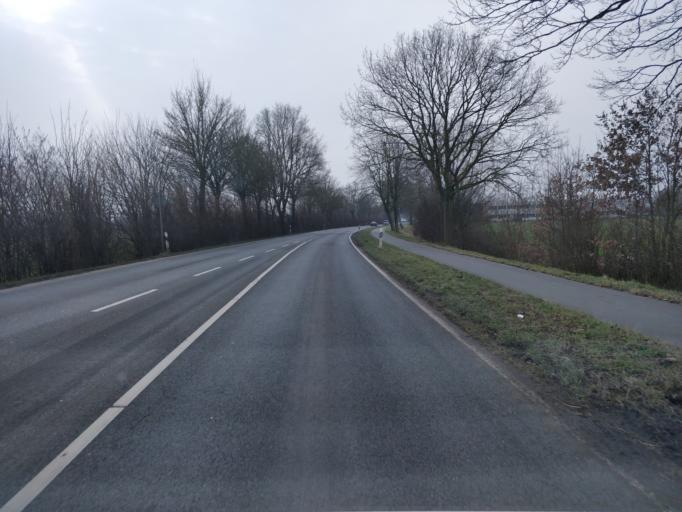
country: DE
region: North Rhine-Westphalia
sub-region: Regierungsbezirk Dusseldorf
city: Emmerich
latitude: 51.8379
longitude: 6.2763
